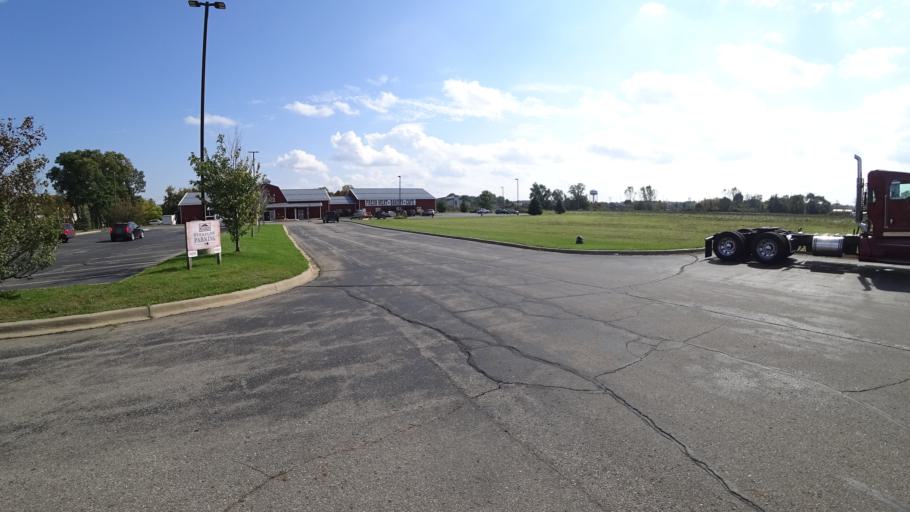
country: US
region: Michigan
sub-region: Saint Joseph County
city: Three Rivers
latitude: 41.9385
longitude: -85.6511
